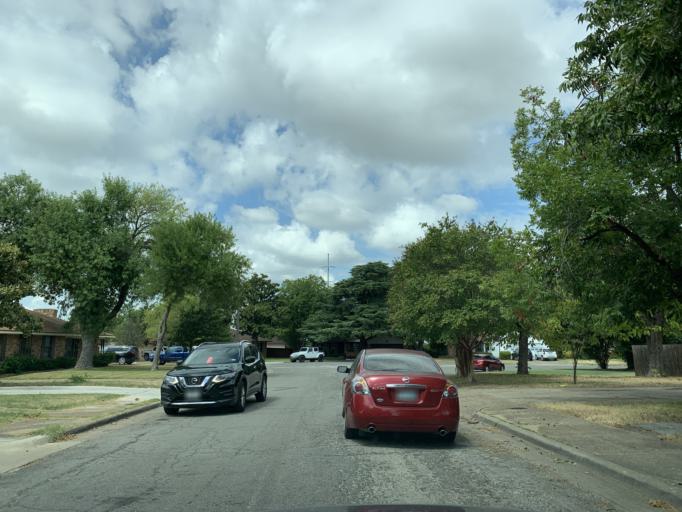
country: US
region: Texas
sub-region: Dallas County
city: Cockrell Hill
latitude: 32.7606
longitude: -96.8714
